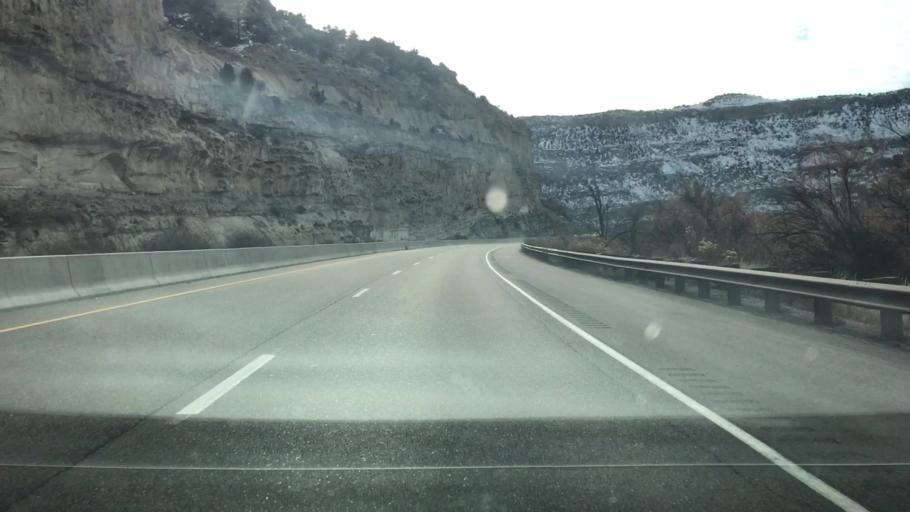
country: US
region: Colorado
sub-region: Mesa County
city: Palisade
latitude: 39.2501
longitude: -108.2571
